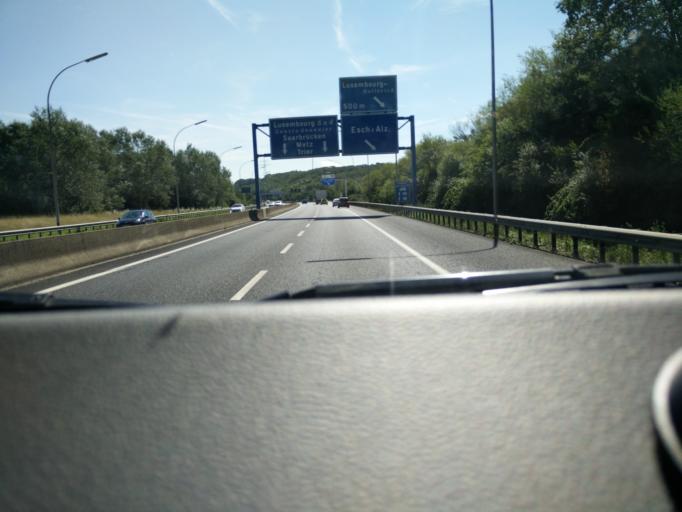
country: LU
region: Luxembourg
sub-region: Canton d'Esch-sur-Alzette
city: Leudelange
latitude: 49.5890
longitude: 6.0840
